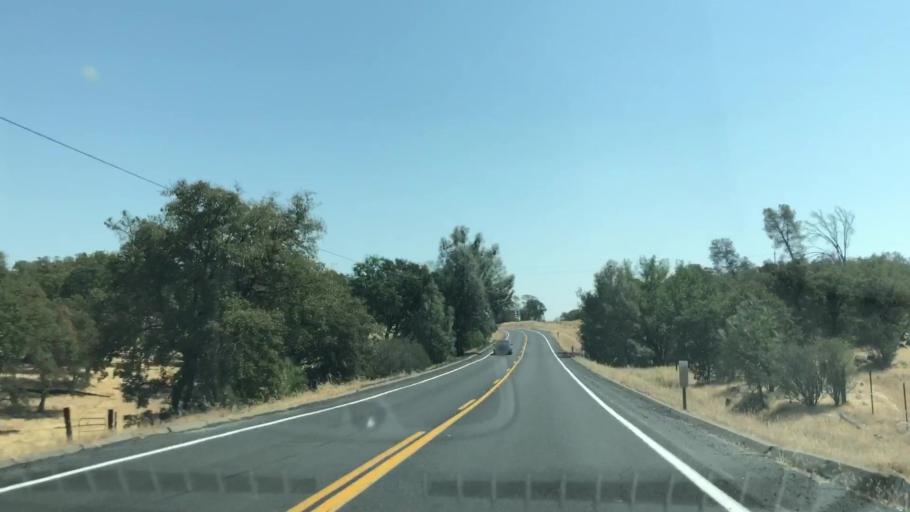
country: US
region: California
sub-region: Calaveras County
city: Copperopolis
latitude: 37.8947
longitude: -120.5529
